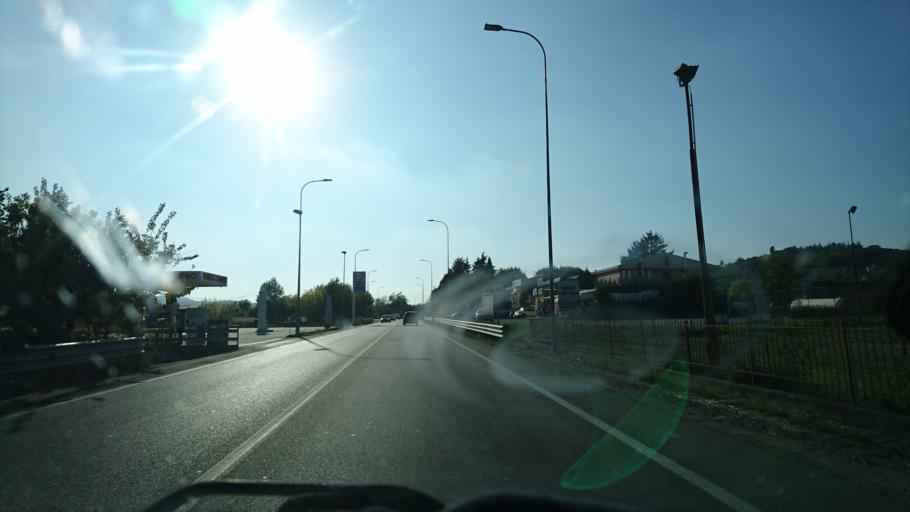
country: IT
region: Piedmont
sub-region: Provincia di Alessandria
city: Visone
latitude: 44.6810
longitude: 8.4998
